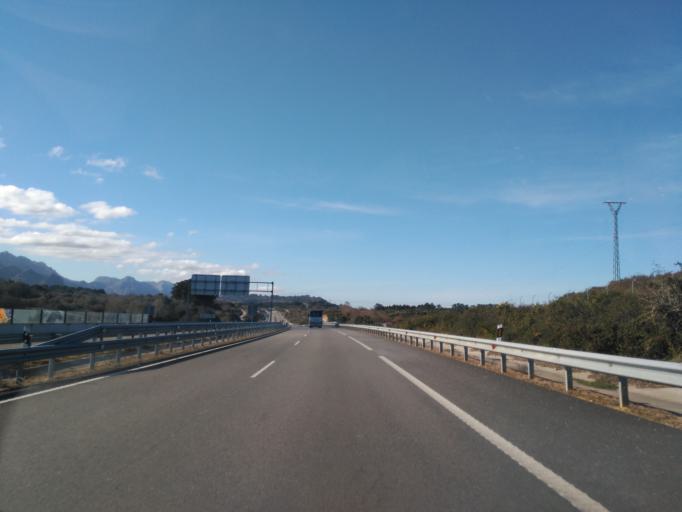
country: ES
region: Asturias
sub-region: Province of Asturias
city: Llanes
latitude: 43.4001
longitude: -4.6641
